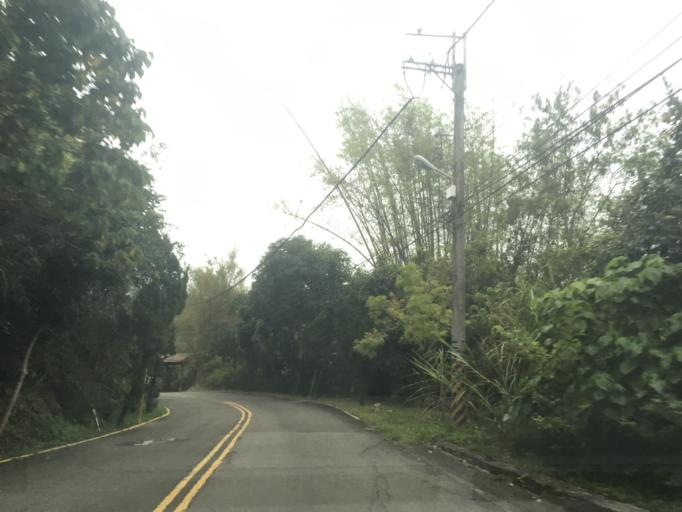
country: TW
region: Taiwan
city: Zhongxing New Village
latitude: 24.0342
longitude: 120.7434
